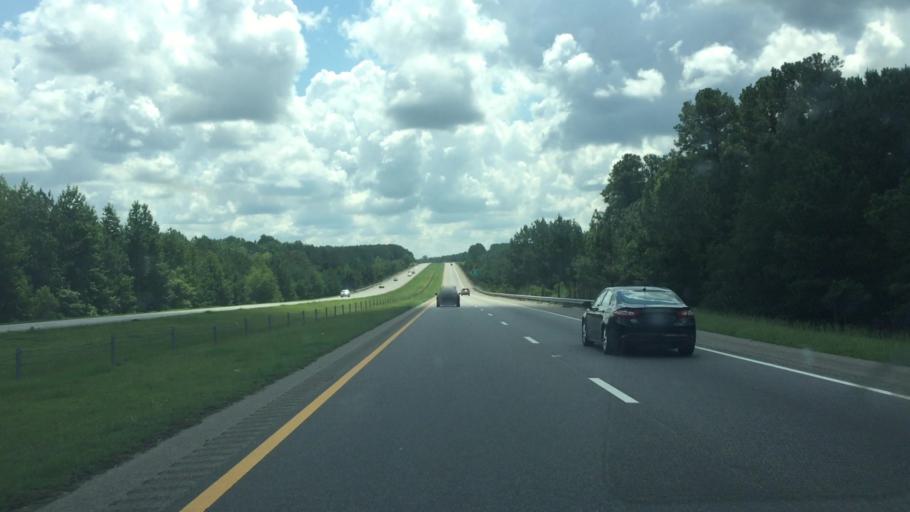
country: US
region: North Carolina
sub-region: Richmond County
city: East Rockingham
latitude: 34.8805
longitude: -79.7789
